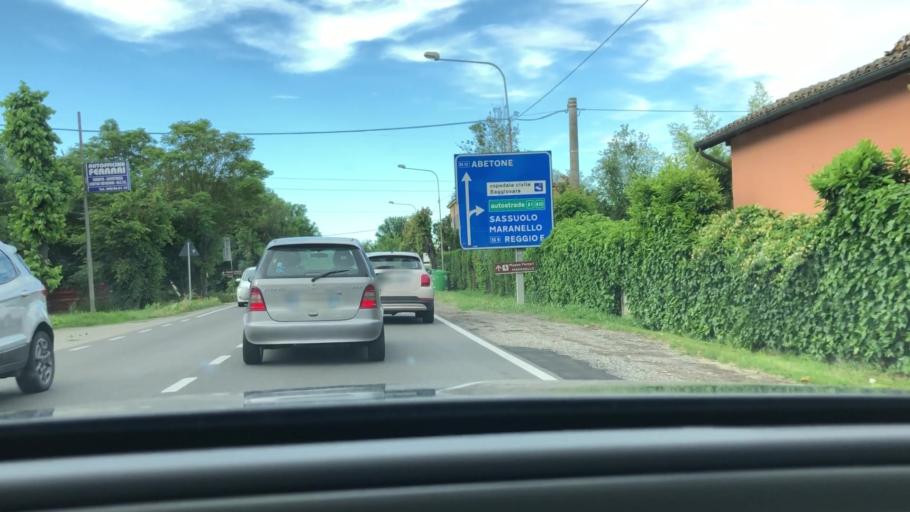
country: IT
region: Emilia-Romagna
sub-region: Provincia di Modena
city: Montale
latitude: 44.6028
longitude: 10.9317
